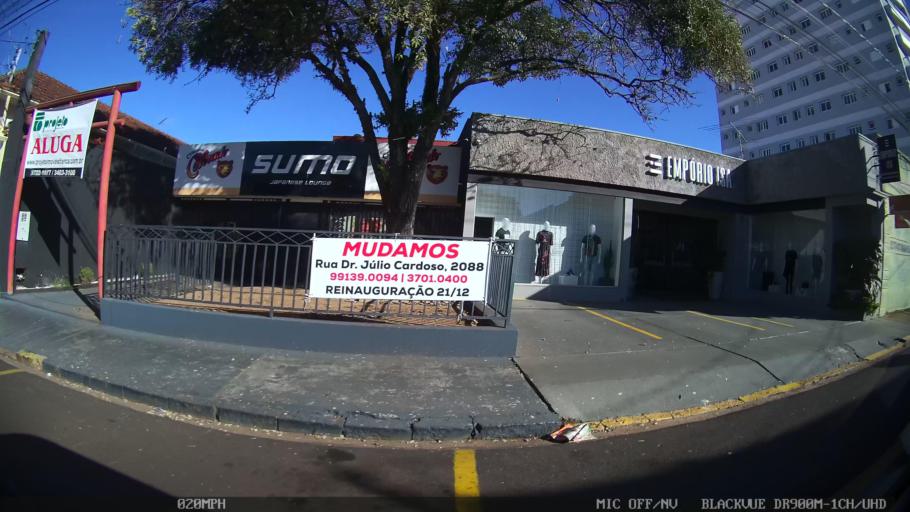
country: BR
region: Sao Paulo
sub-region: Franca
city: Franca
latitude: -20.5333
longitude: -47.4002
